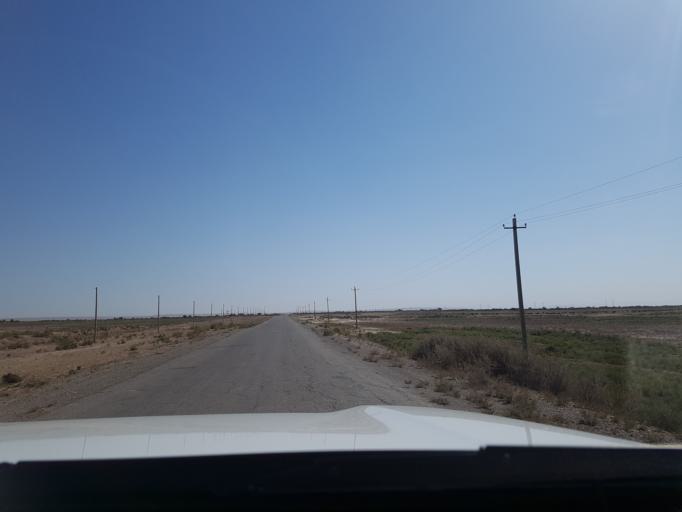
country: IR
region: Razavi Khorasan
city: Sarakhs
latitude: 36.5036
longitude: 61.2535
